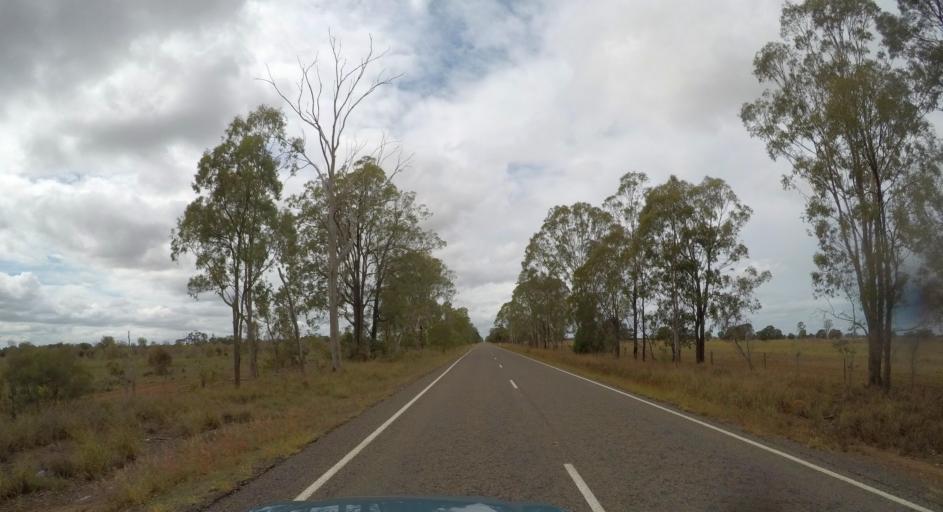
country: AU
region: Queensland
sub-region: South Burnett
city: Kingaroy
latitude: -26.3906
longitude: 151.2063
